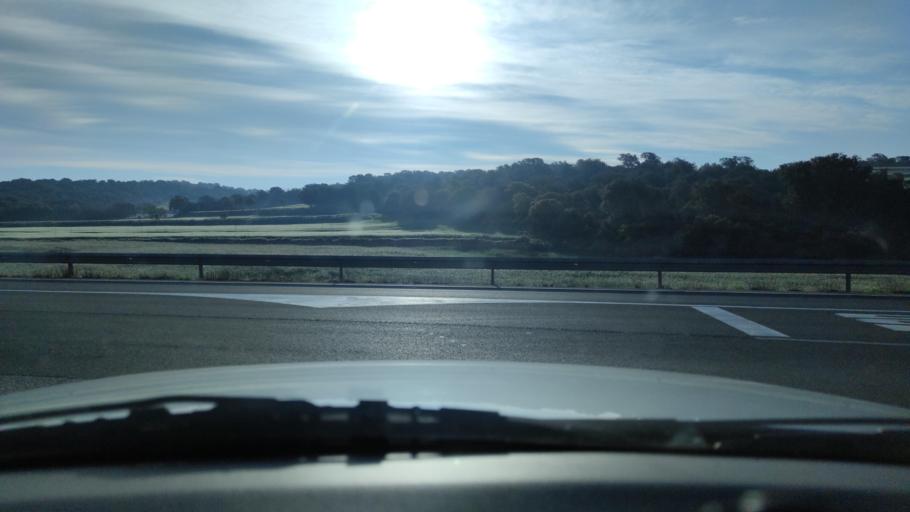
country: ES
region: Catalonia
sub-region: Provincia de Lleida
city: Agramunt
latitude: 41.8276
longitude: 1.0634
